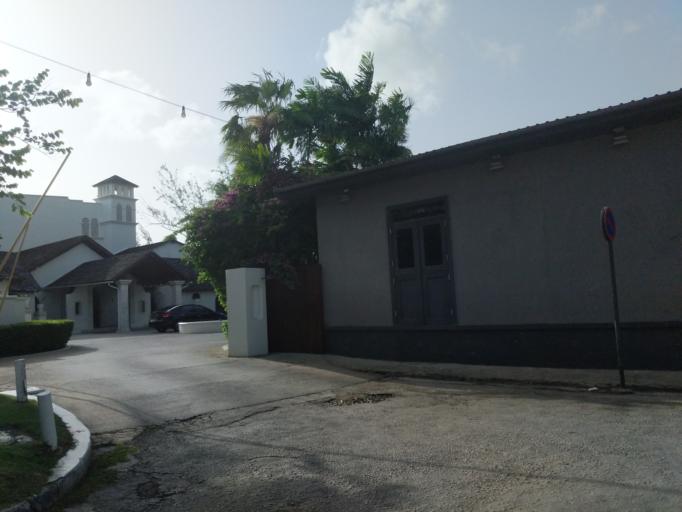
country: BB
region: Saint James
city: Holetown
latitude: 13.1870
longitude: -59.6371
